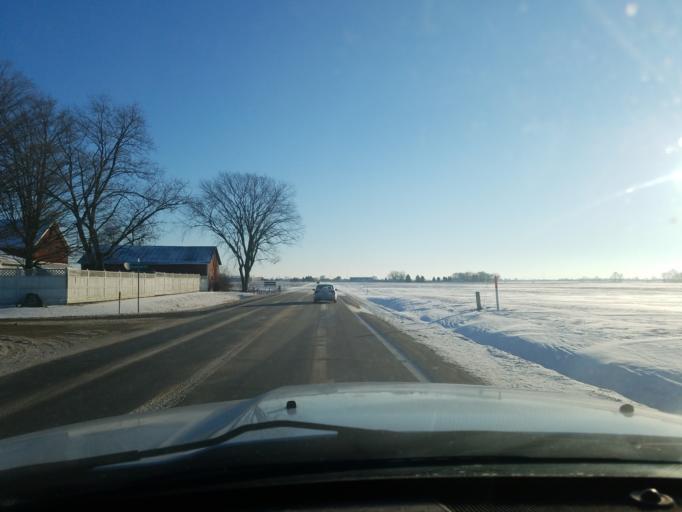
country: US
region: Indiana
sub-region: Noble County
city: Ligonier
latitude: 41.4518
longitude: -85.6155
